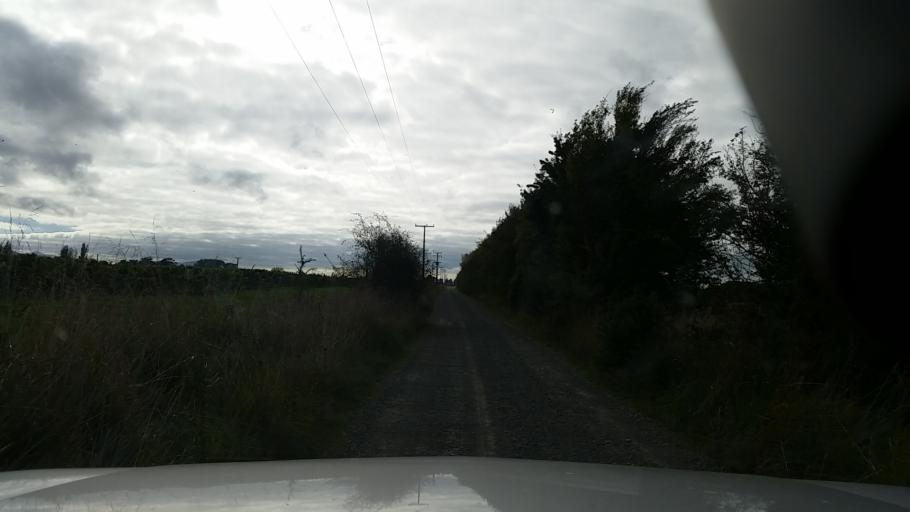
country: NZ
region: Marlborough
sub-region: Marlborough District
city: Blenheim
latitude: -41.4655
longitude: 173.9871
